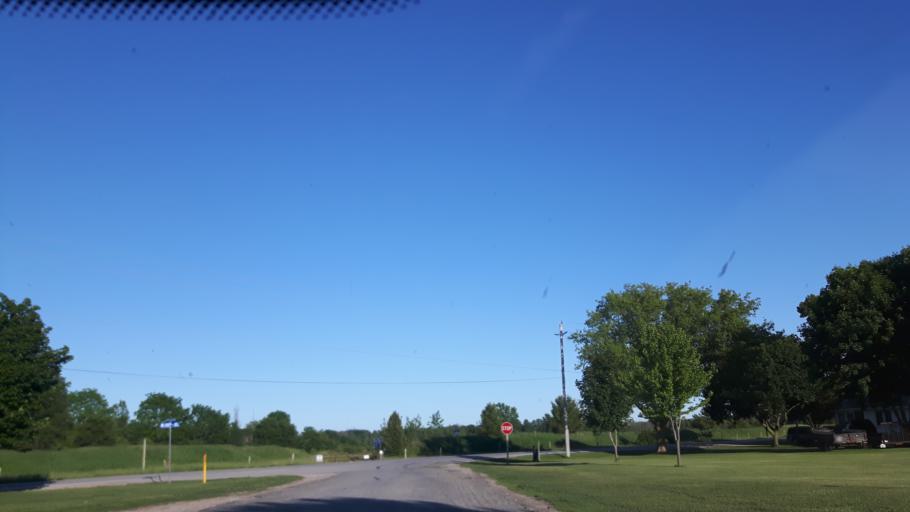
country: CA
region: Ontario
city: Goderich
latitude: 43.6436
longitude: -81.6030
